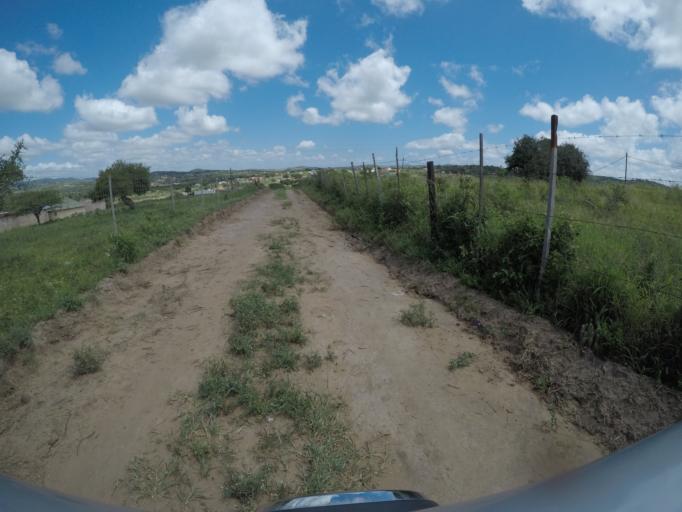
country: ZA
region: KwaZulu-Natal
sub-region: uThungulu District Municipality
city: Empangeni
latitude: -28.5826
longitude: 31.8439
